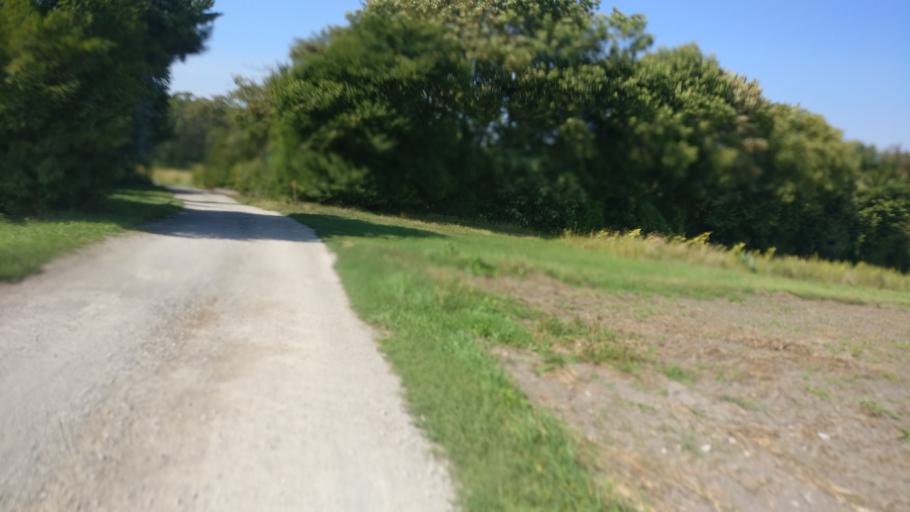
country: AT
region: Lower Austria
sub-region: Politischer Bezirk Wien-Umgebung
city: Moosbrunn
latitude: 47.9926
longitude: 16.4161
